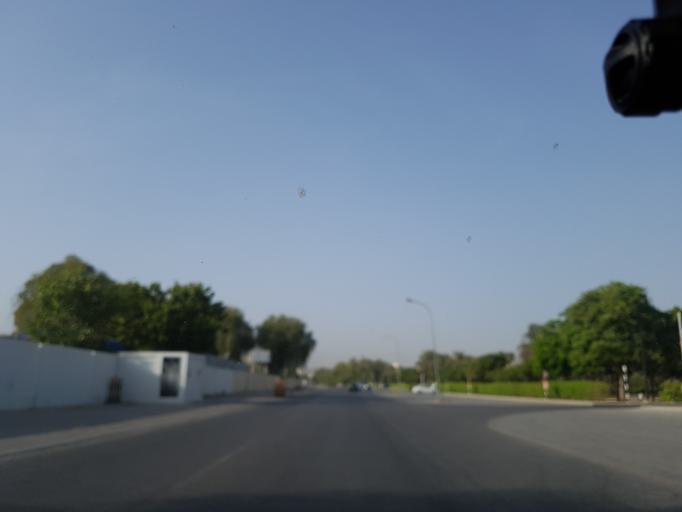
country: OM
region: Muhafazat Masqat
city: Bawshar
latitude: 23.5831
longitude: 58.3926
